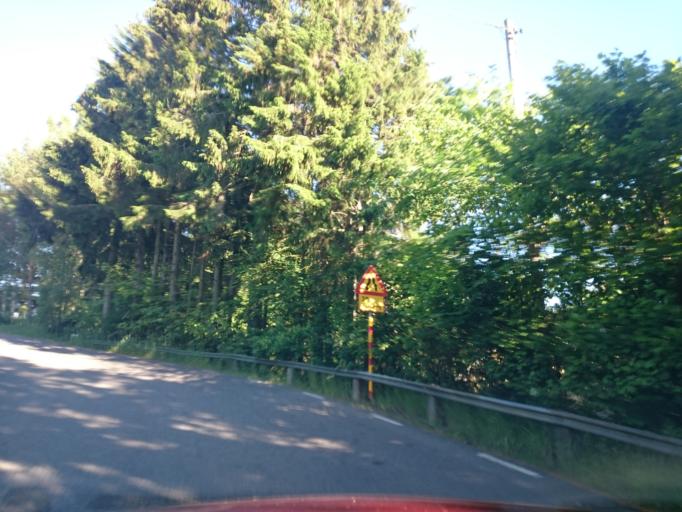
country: SE
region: Vaestra Goetaland
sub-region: Lerums Kommun
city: Stenkullen
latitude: 57.7864
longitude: 12.3141
